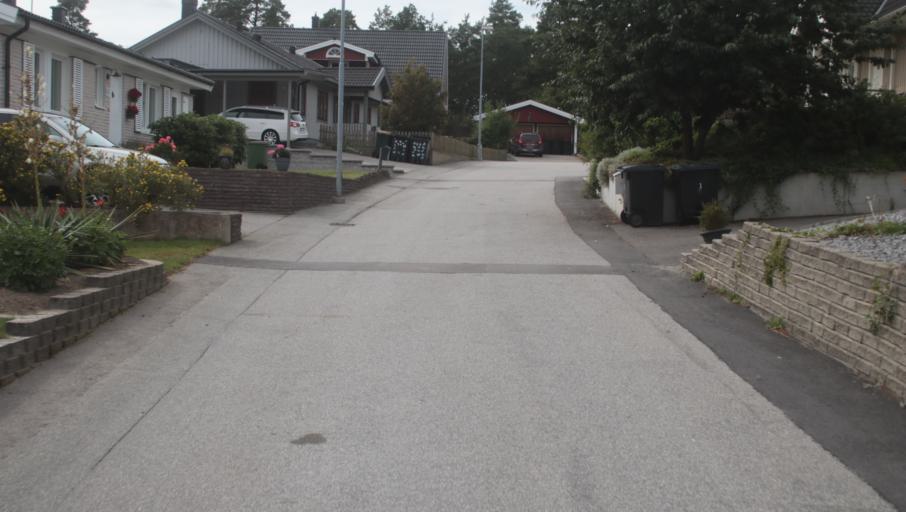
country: SE
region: Blekinge
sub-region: Karlshamns Kommun
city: Karlshamn
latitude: 56.2053
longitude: 14.8590
